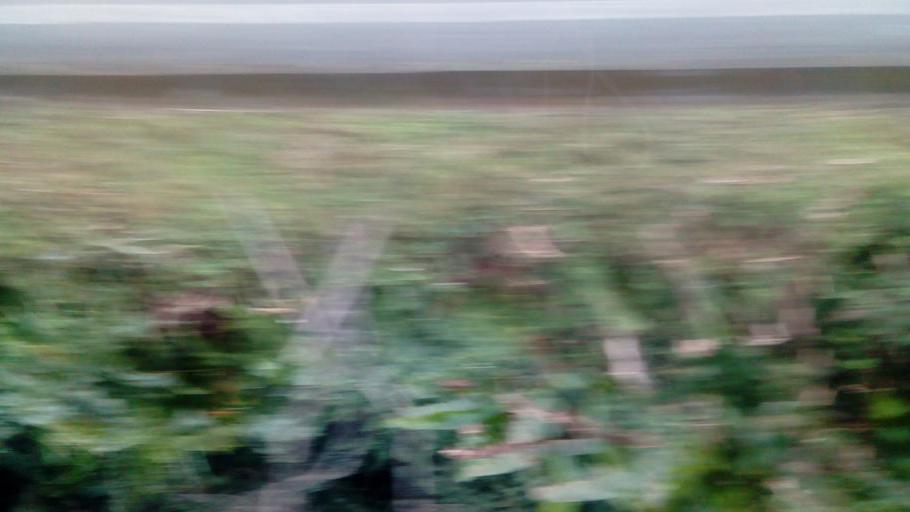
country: TW
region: Taiwan
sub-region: Yilan
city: Yilan
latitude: 24.5579
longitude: 121.4773
